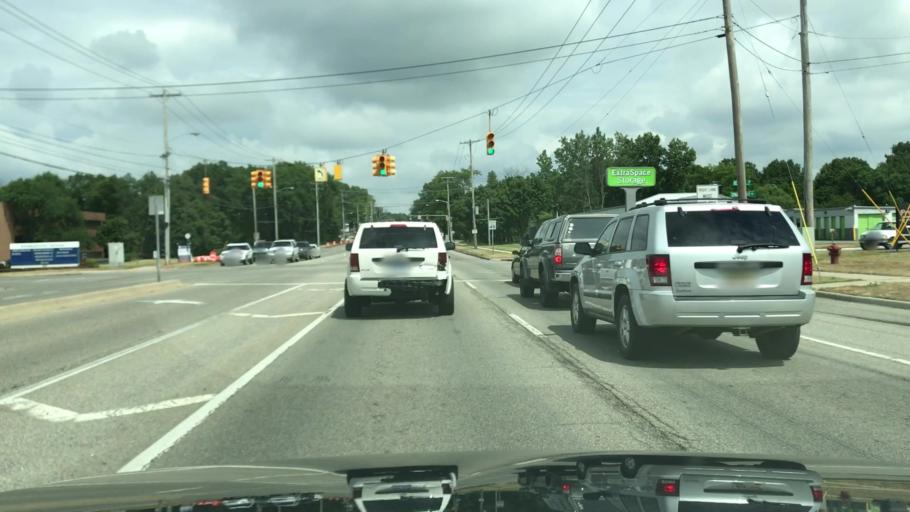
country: US
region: Michigan
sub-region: Kent County
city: Grandville
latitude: 42.8846
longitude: -85.7367
